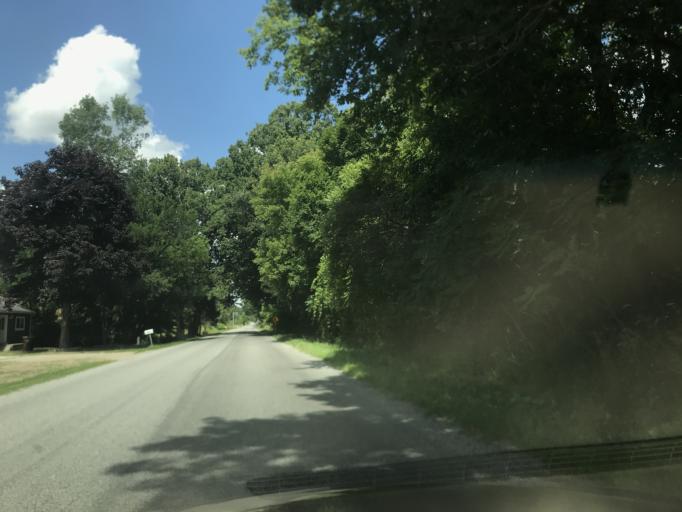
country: US
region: Michigan
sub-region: Ingham County
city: Holt
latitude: 42.6230
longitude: -84.5626
